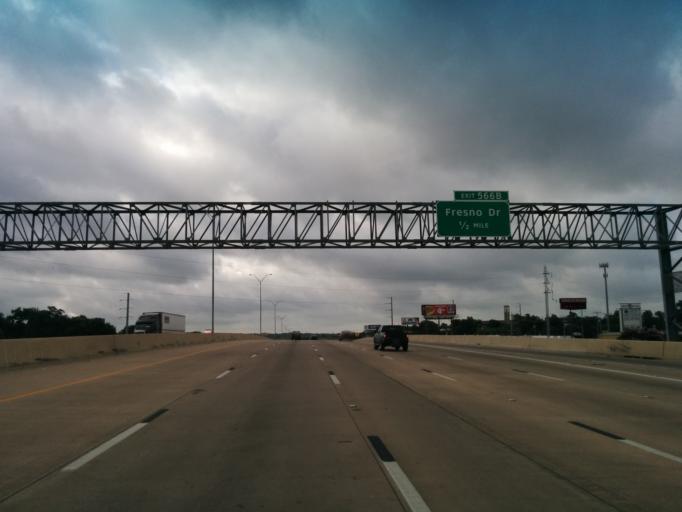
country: US
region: Texas
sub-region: Bexar County
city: Balcones Heights
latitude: 29.4823
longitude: -98.5271
